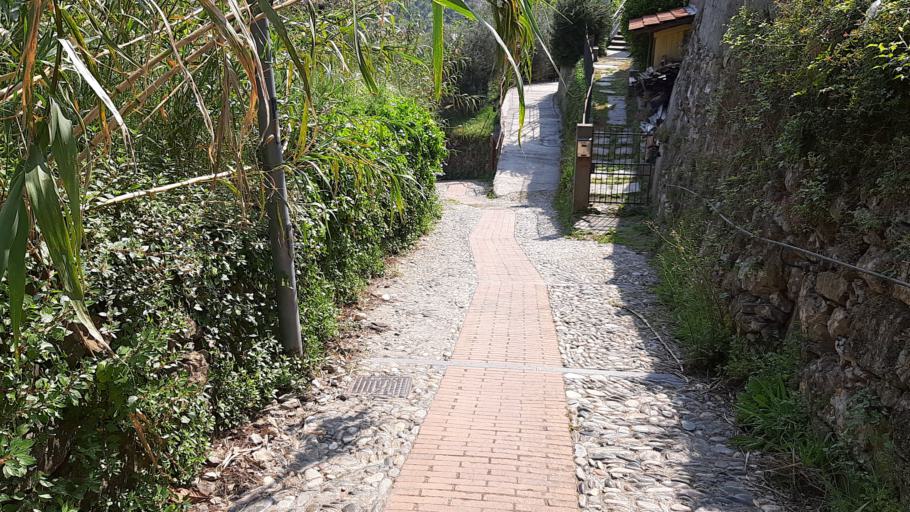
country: IT
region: Liguria
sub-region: Provincia di Genova
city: Bogliasco
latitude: 44.4275
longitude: 9.0166
